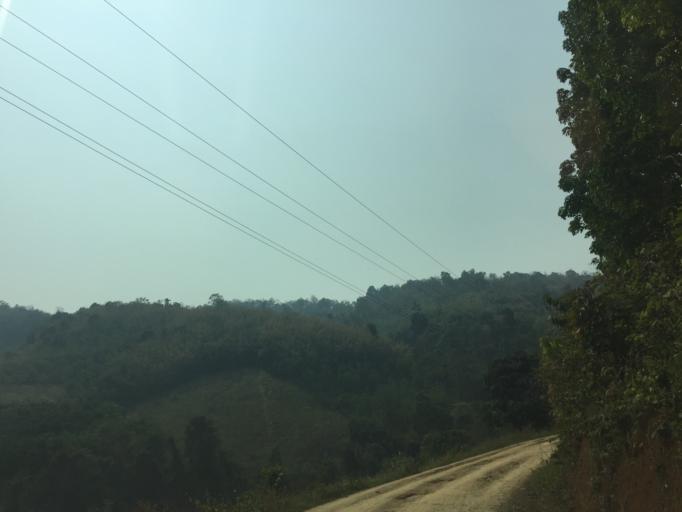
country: TH
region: Phayao
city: Phu Sang
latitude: 19.6005
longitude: 100.5337
